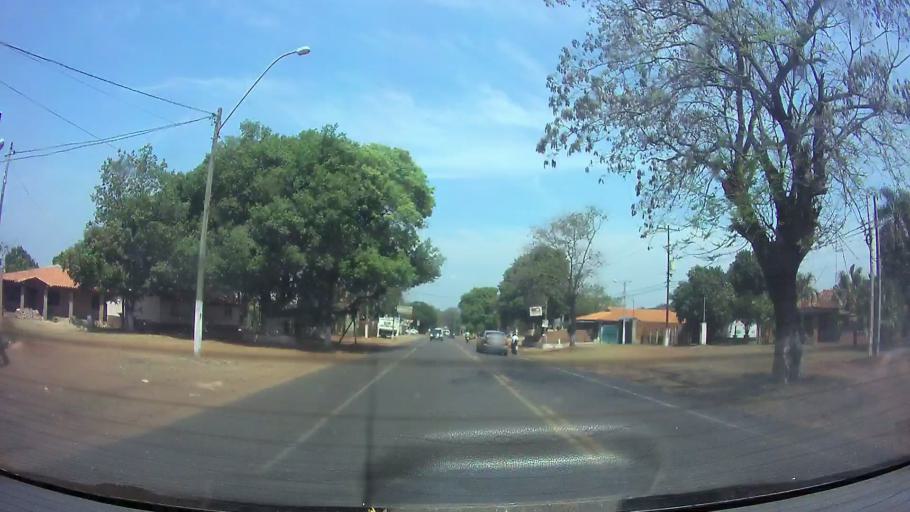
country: PY
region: Central
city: Capiata
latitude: -25.4096
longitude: -57.4600
